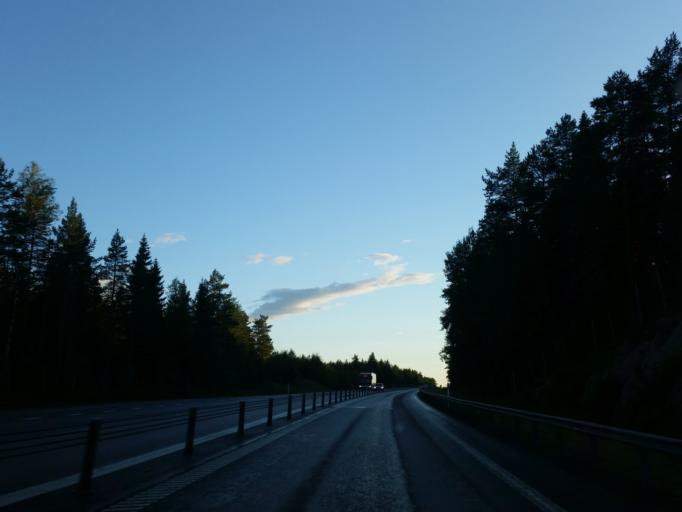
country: SE
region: Vaesterbotten
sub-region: Umea Kommun
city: Saevar
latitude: 63.9046
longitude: 20.5792
